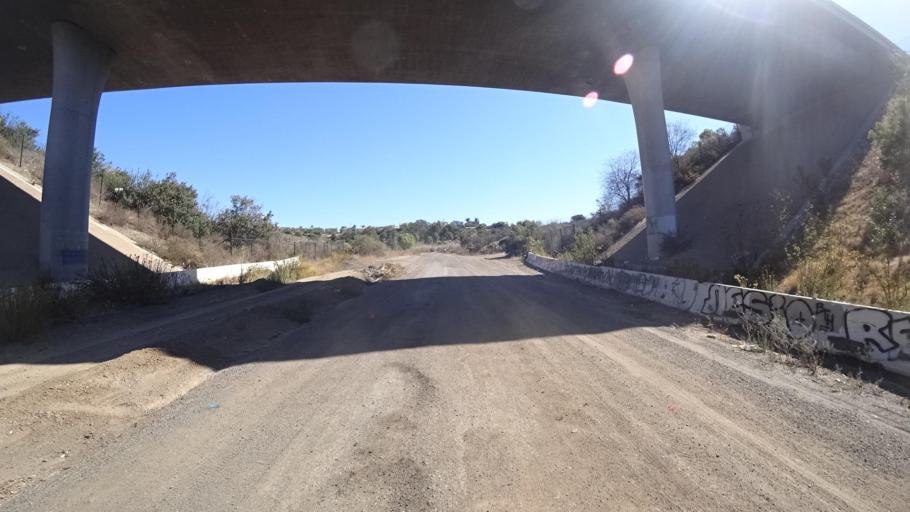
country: US
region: California
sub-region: San Diego County
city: La Presa
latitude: 32.6655
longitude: -116.9836
